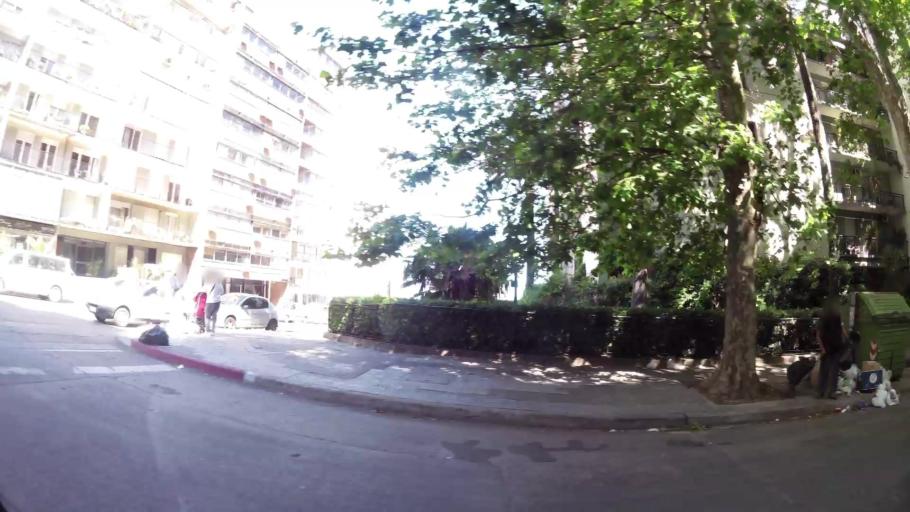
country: UY
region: Montevideo
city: Montevideo
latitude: -34.9126
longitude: -56.1478
